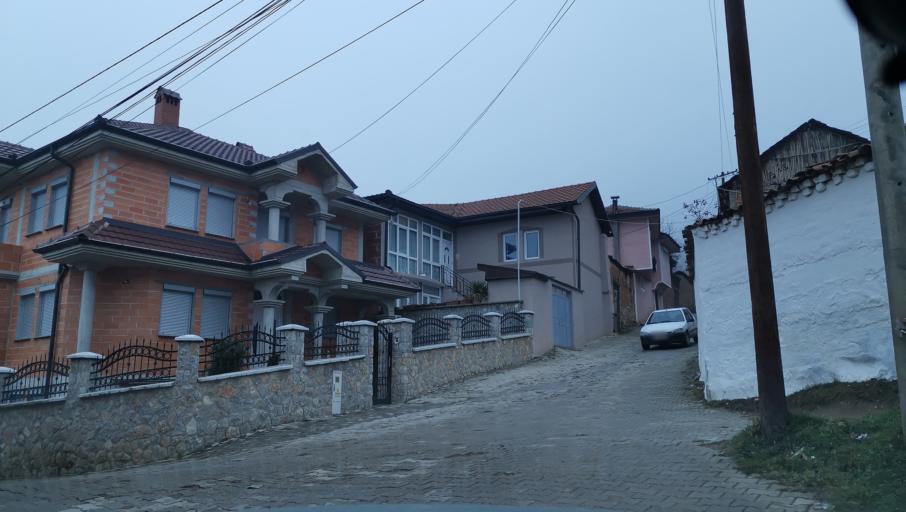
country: MK
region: Debar
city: Debar
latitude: 41.5268
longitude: 20.5281
